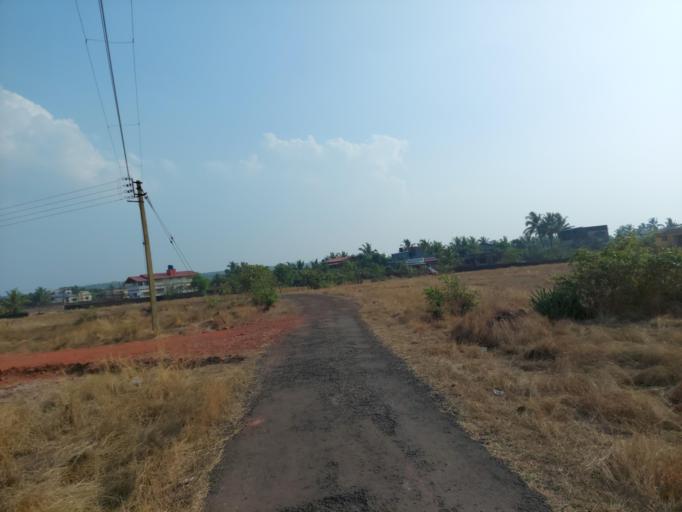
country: IN
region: Maharashtra
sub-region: Ratnagiri
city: Ratnagiri
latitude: 16.9357
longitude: 73.3246
